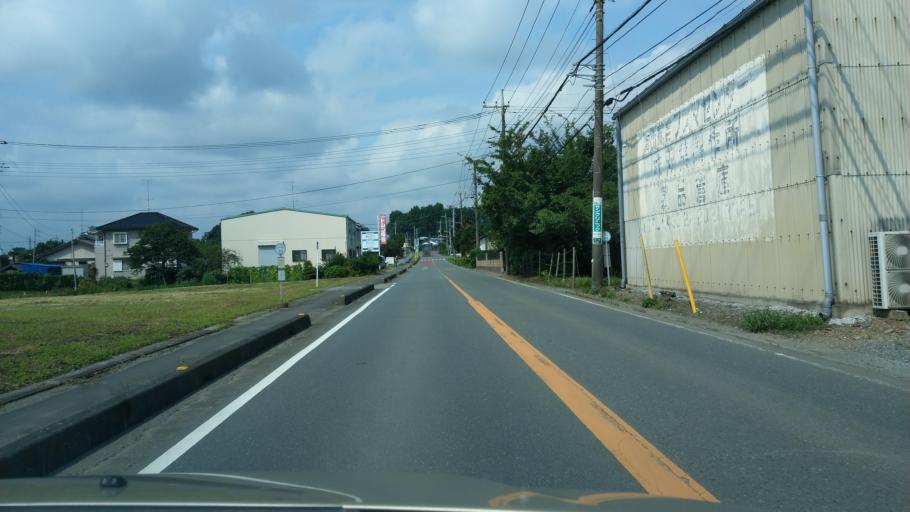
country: JP
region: Saitama
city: Sakado
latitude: 36.0262
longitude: 139.3736
